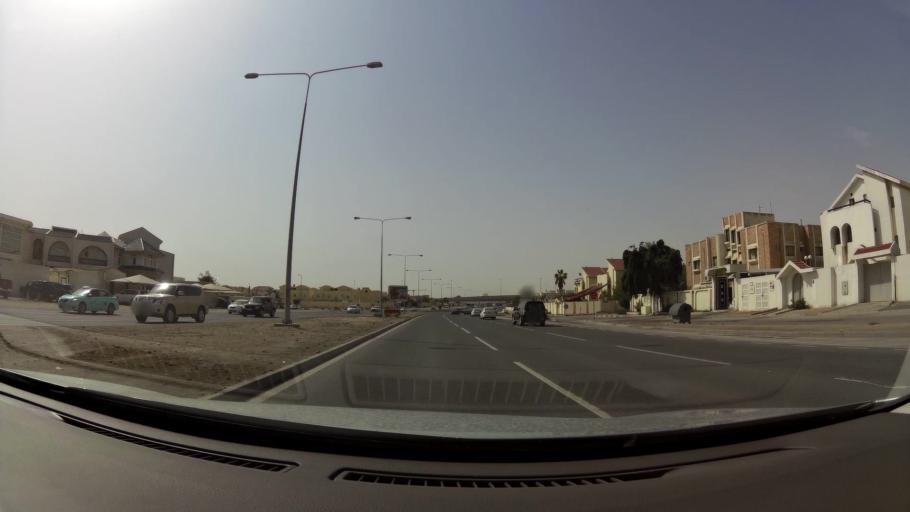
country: QA
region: Baladiyat ad Dawhah
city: Doha
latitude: 25.2421
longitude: 51.5240
